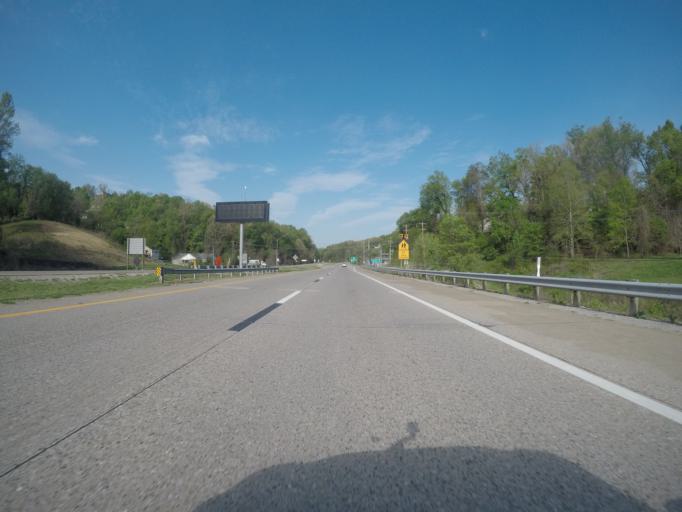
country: US
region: West Virginia
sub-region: Kanawha County
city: South Charleston
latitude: 38.3405
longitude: -81.6830
